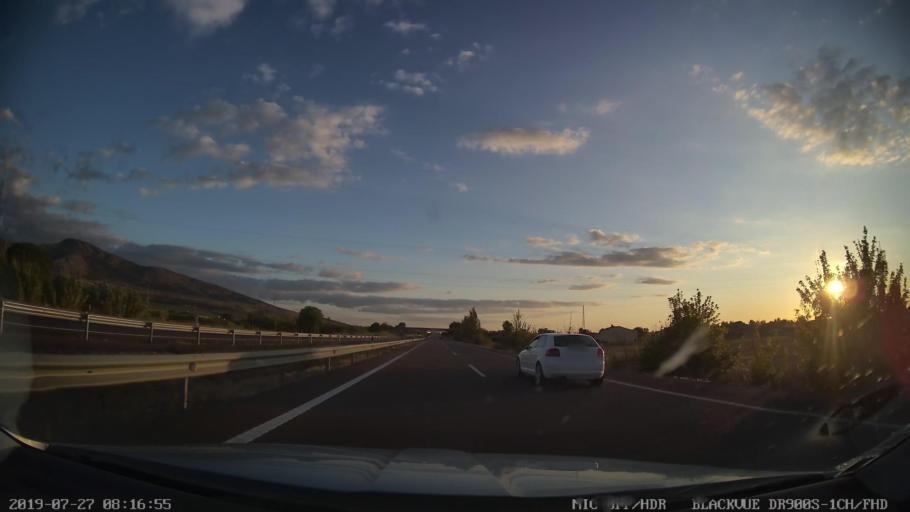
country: ES
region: Extremadura
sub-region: Provincia de Badajoz
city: Calamonte
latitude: 38.8914
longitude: -6.4254
